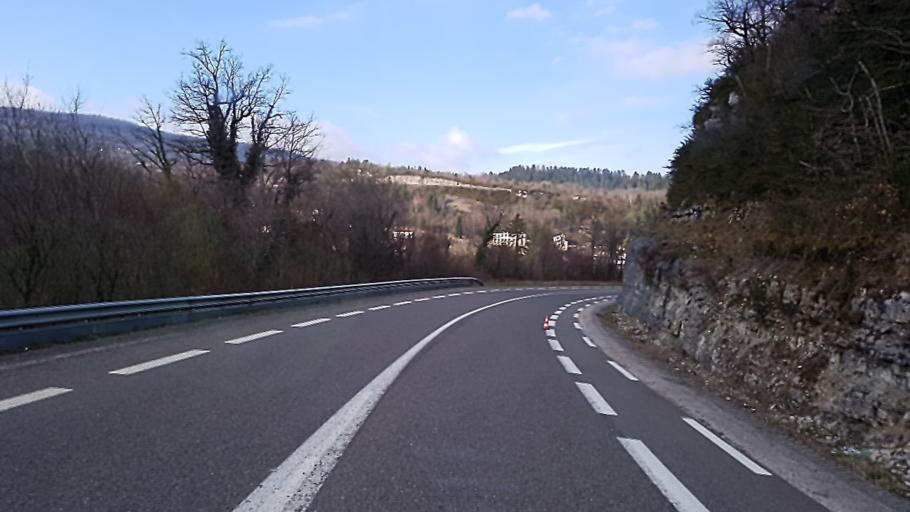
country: FR
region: Franche-Comte
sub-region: Departement du Jura
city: Lavans-les-Saint-Claude
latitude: 46.3792
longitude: 5.7960
